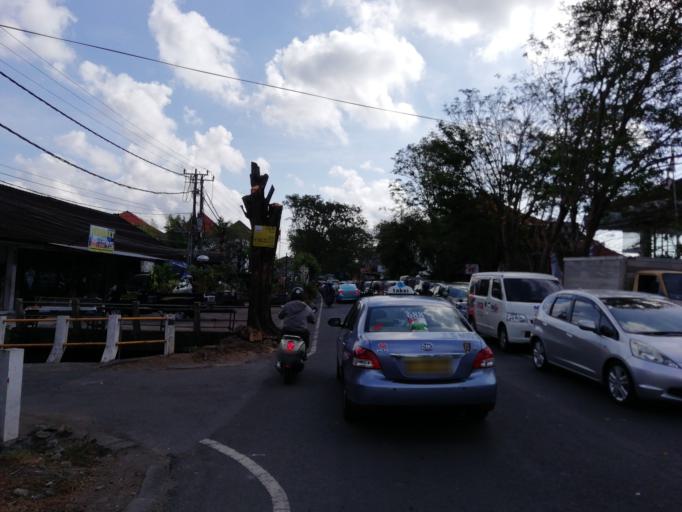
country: ID
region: Bali
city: Karyadharma
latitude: -8.6938
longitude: 115.1880
